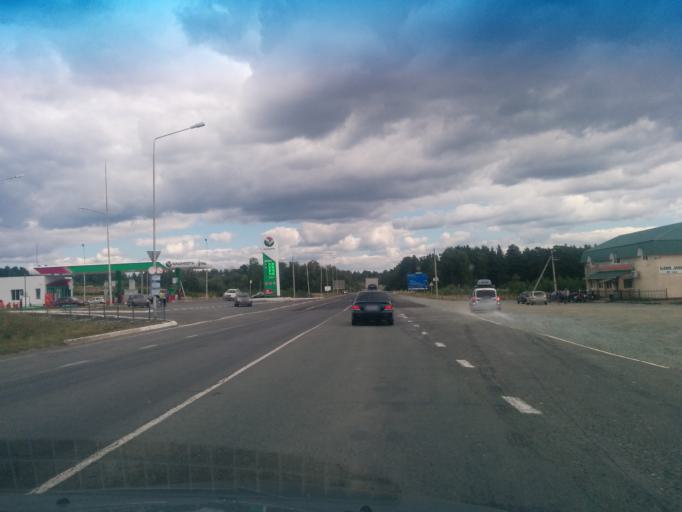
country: RU
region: Bashkortostan
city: Lomovka
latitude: 53.8980
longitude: 58.0792
